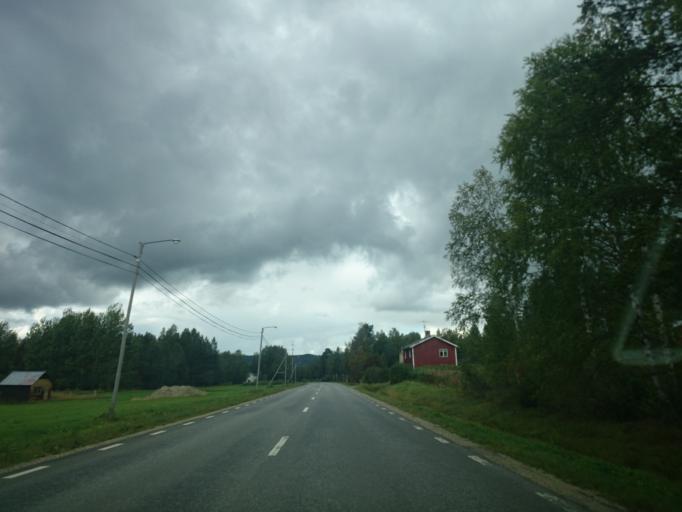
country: SE
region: Jaemtland
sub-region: Bergs Kommun
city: Hoverberg
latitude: 62.4890
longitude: 14.7394
